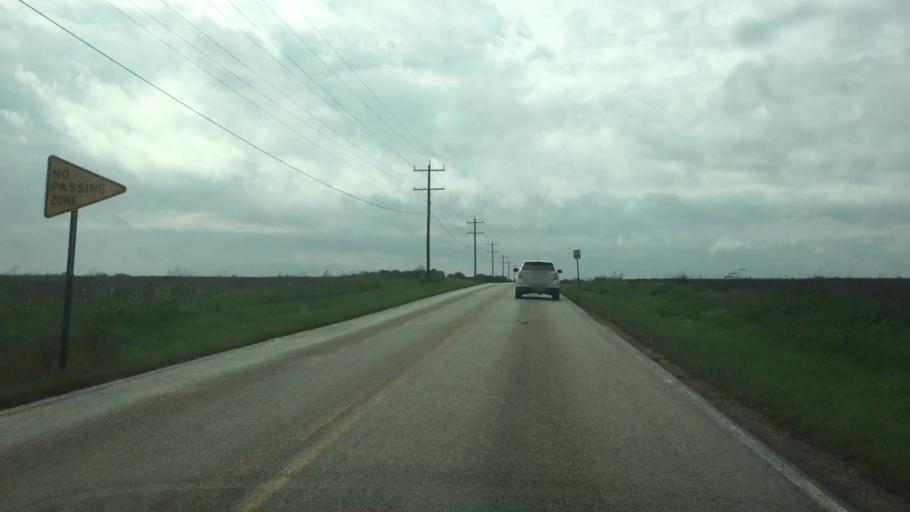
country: US
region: Kansas
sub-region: Allen County
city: Humboldt
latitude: 37.8489
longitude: -95.4369
